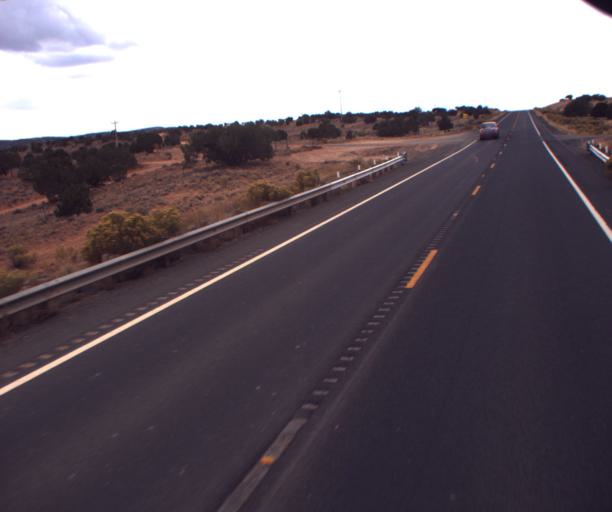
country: US
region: Arizona
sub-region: Coconino County
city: Kaibito
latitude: 36.4492
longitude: -110.7205
